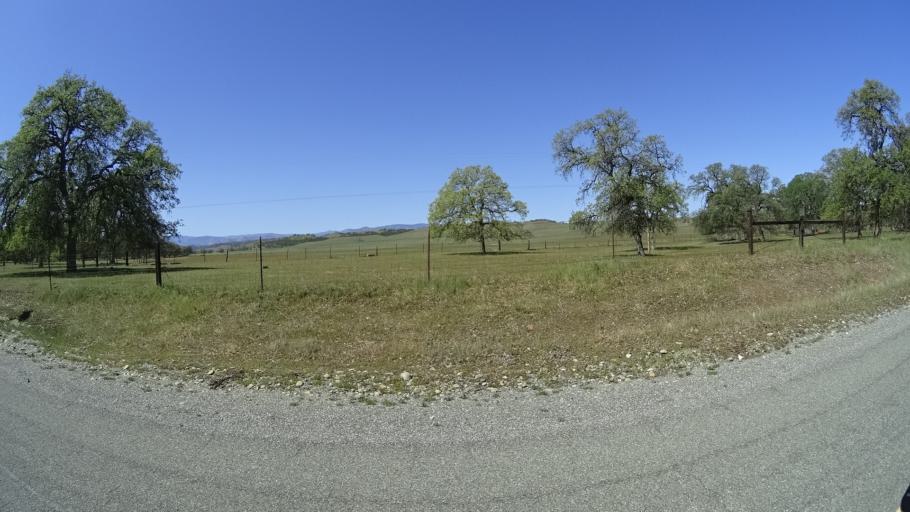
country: US
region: California
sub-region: Glenn County
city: Orland
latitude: 39.7335
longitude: -122.4143
